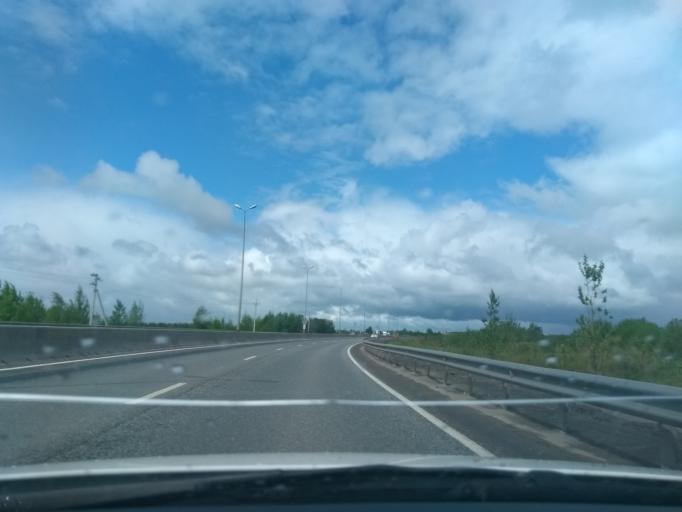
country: RU
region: Perm
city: Kondratovo
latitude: 57.9996
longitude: 56.0956
